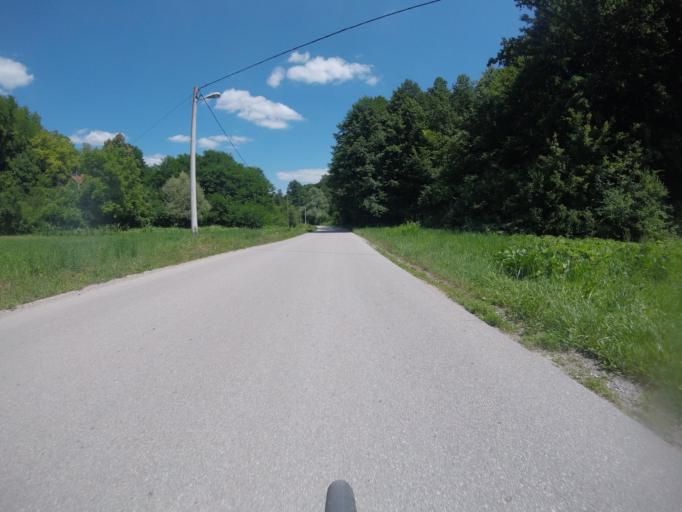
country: HR
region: Karlovacka
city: Ozalj
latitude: 45.6651
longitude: 15.4861
